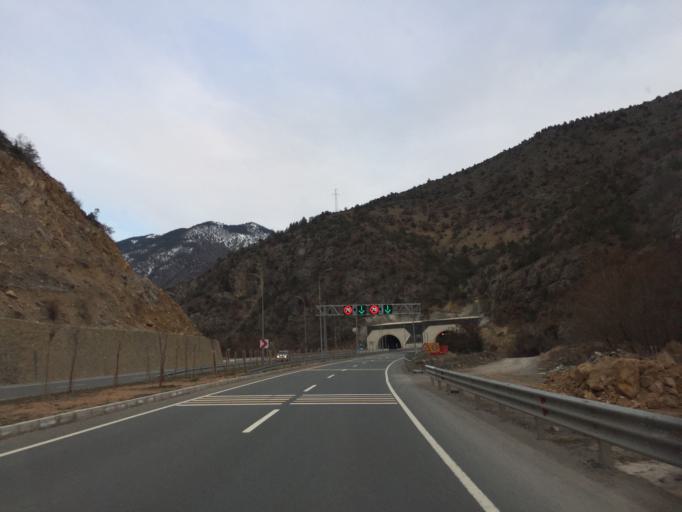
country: TR
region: Gumushane
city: Gumushkhane
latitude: 40.5190
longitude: 39.4094
